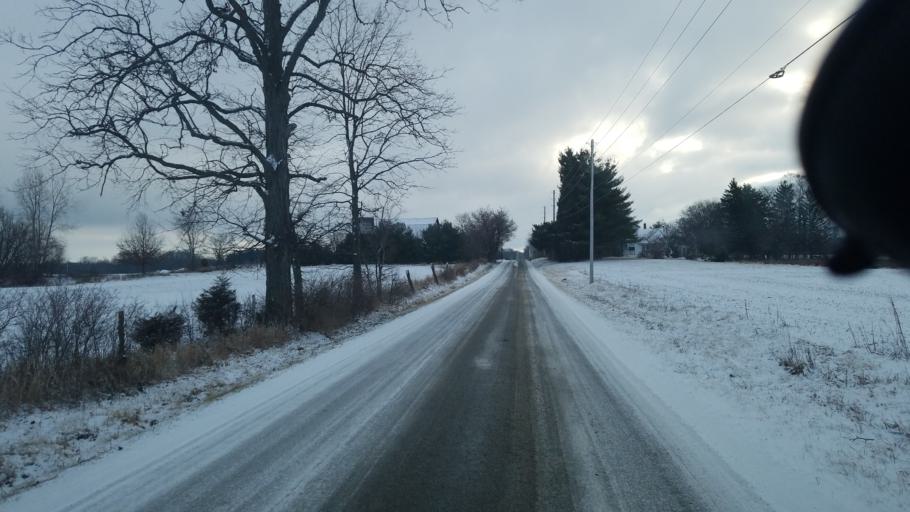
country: US
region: Ohio
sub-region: Morrow County
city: Mount Gilead
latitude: 40.5676
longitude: -82.8540
